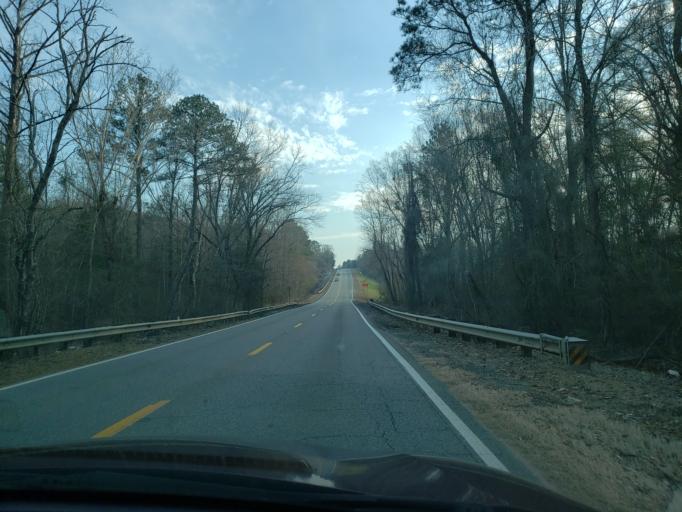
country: US
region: Alabama
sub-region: Hale County
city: Moundville
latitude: 32.9247
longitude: -87.6372
